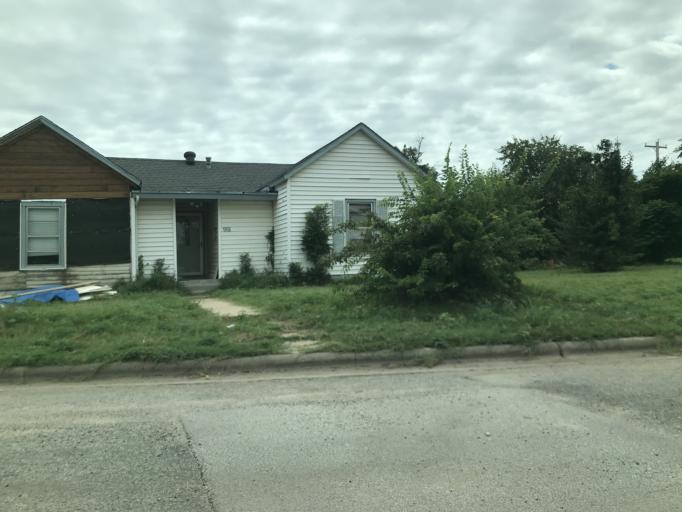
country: US
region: Texas
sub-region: Taylor County
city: Abilene
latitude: 32.4393
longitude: -99.7362
